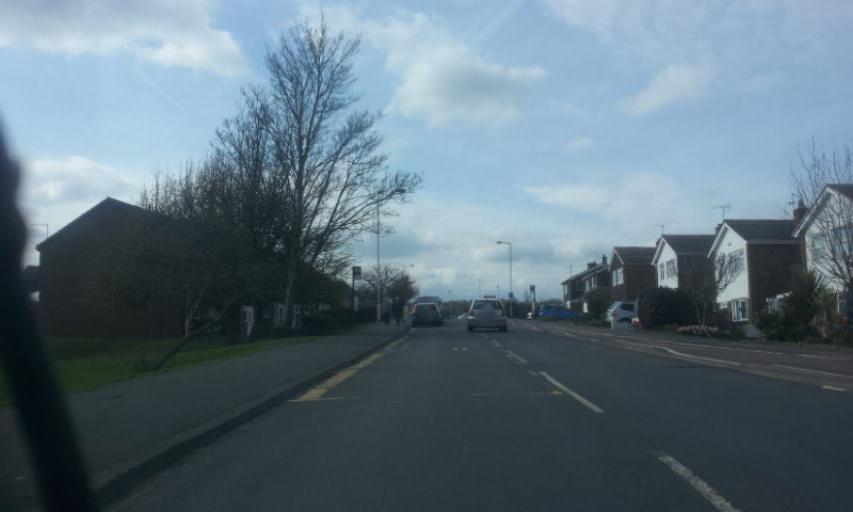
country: GB
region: England
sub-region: Kent
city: Faversham
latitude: 51.3217
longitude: 0.8774
